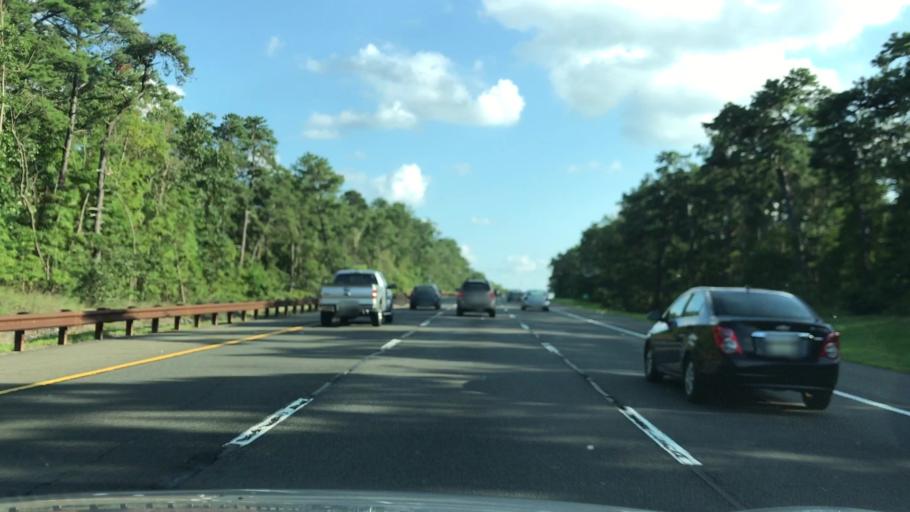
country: US
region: New Jersey
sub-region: Ocean County
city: South Toms River
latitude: 39.9311
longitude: -74.2090
